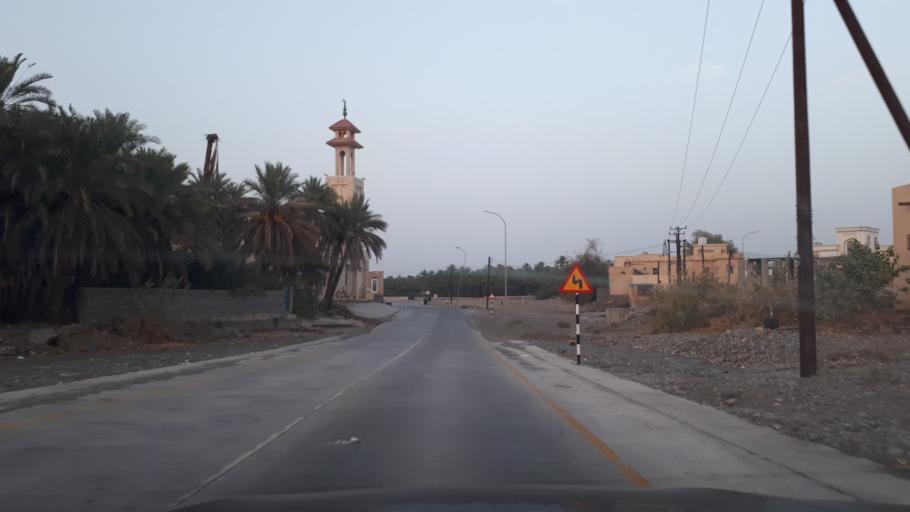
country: OM
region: Al Batinah
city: Rustaq
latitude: 23.5606
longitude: 57.5608
